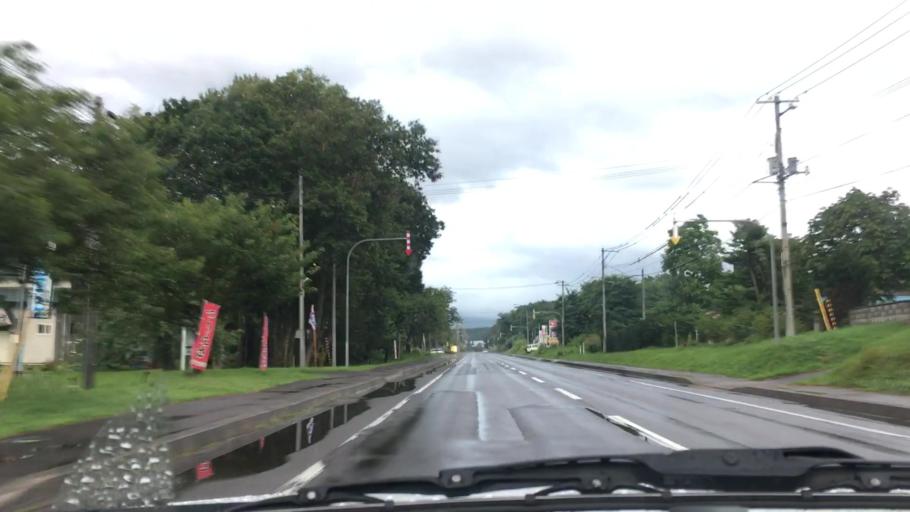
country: JP
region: Hokkaido
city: Nanae
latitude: 42.1099
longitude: 140.5515
